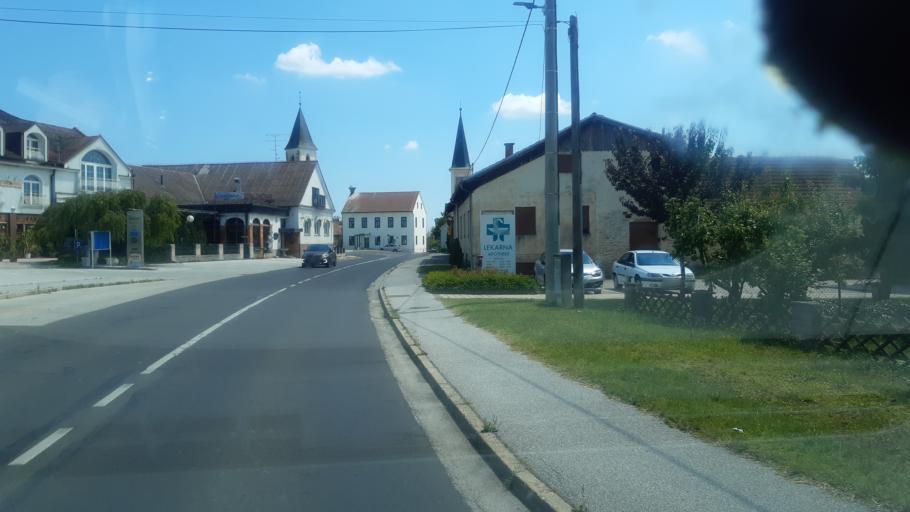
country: SI
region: Moravske Toplice
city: Moravske Toplice
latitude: 46.6855
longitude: 16.1900
